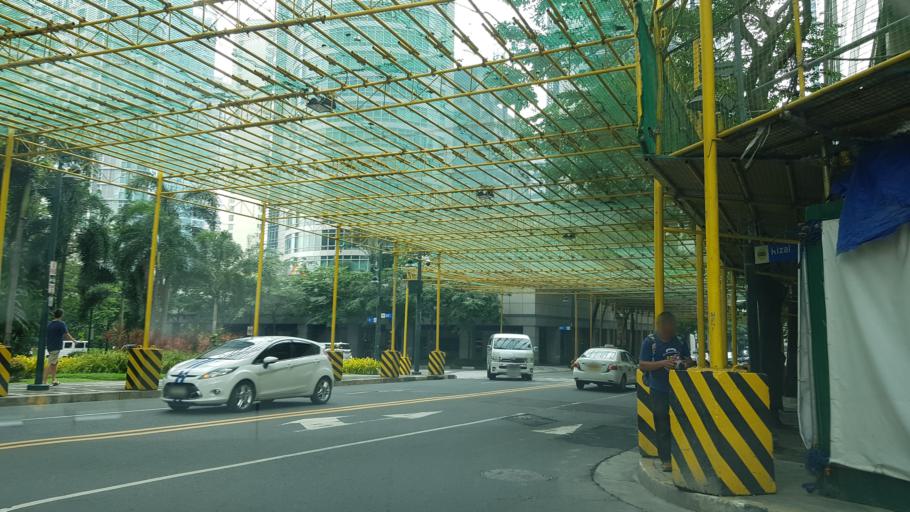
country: PH
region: Metro Manila
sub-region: Makati City
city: Makati City
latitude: 14.5477
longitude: 121.0459
